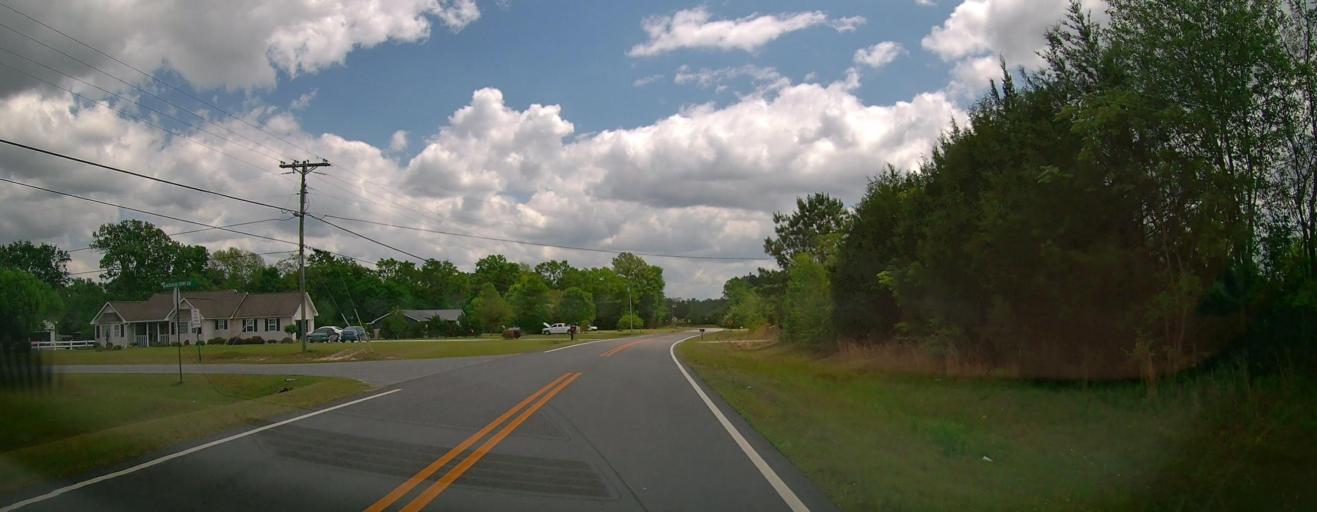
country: US
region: Georgia
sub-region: Laurens County
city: Dublin
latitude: 32.6004
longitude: -82.9608
